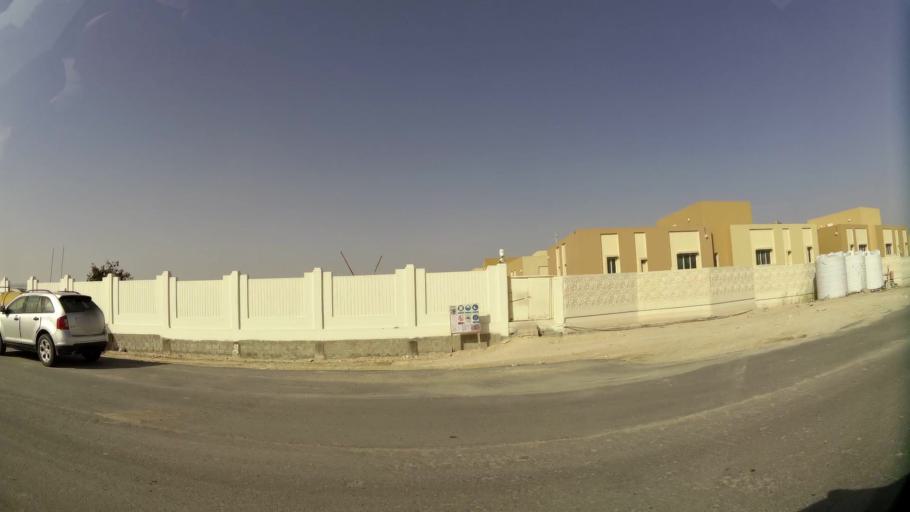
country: QA
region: Baladiyat ar Rayyan
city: Ar Rayyan
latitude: 25.3322
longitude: 51.4169
